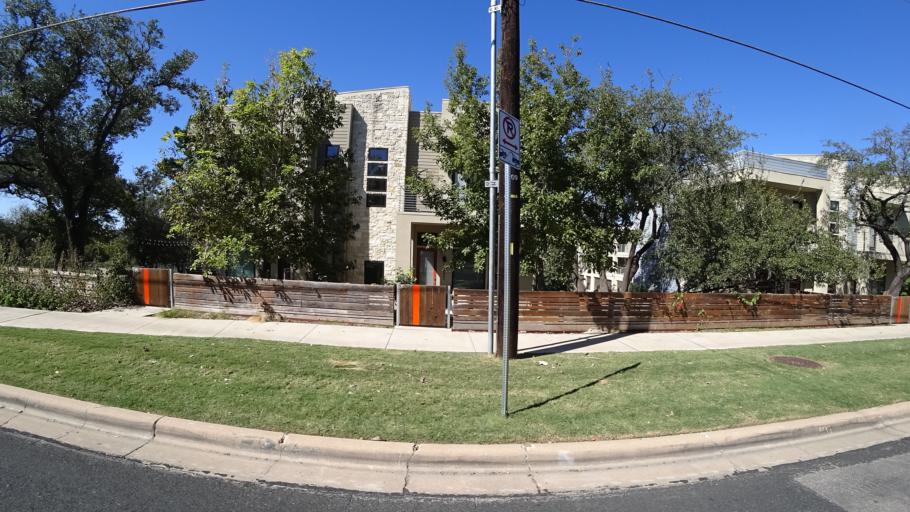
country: US
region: Texas
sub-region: Travis County
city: Austin
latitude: 30.2377
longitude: -97.7673
